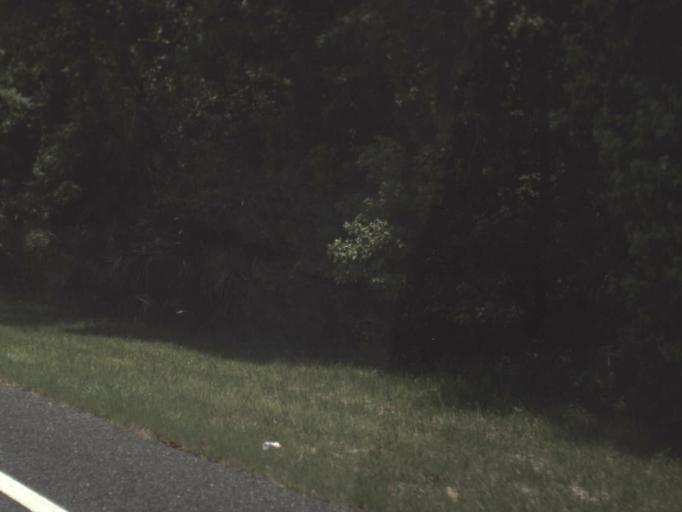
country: US
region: Florida
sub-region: Taylor County
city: Steinhatchee
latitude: 29.6869
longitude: -83.2682
